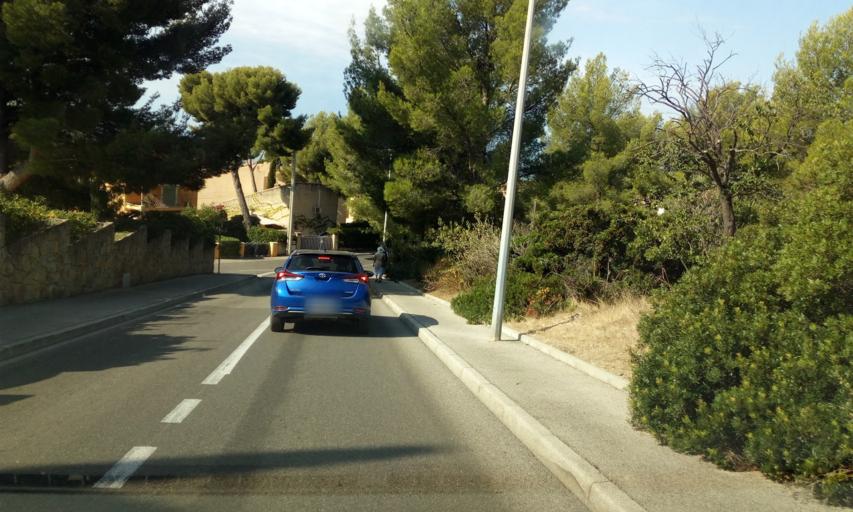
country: FR
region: Provence-Alpes-Cote d'Azur
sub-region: Departement du Var
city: Bandol
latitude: 43.1431
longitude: 5.7595
